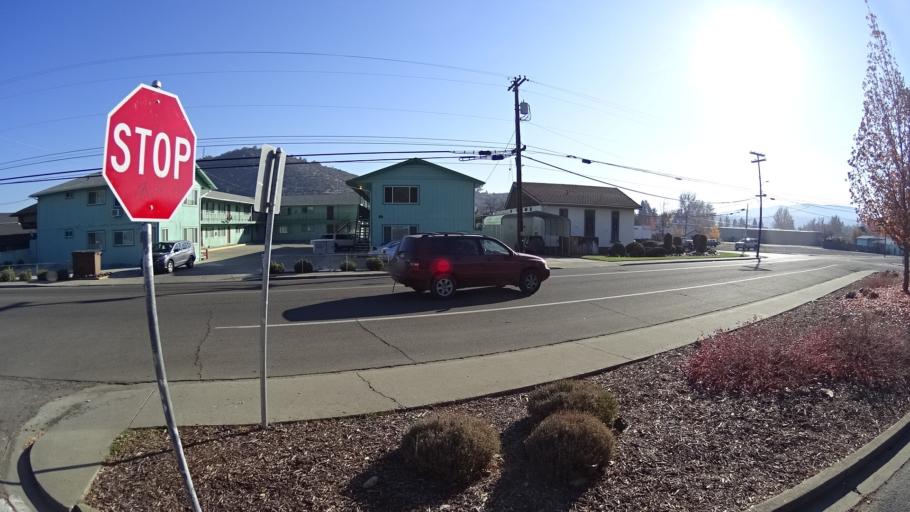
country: US
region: California
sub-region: Siskiyou County
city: Yreka
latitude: 41.7212
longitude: -122.6419
